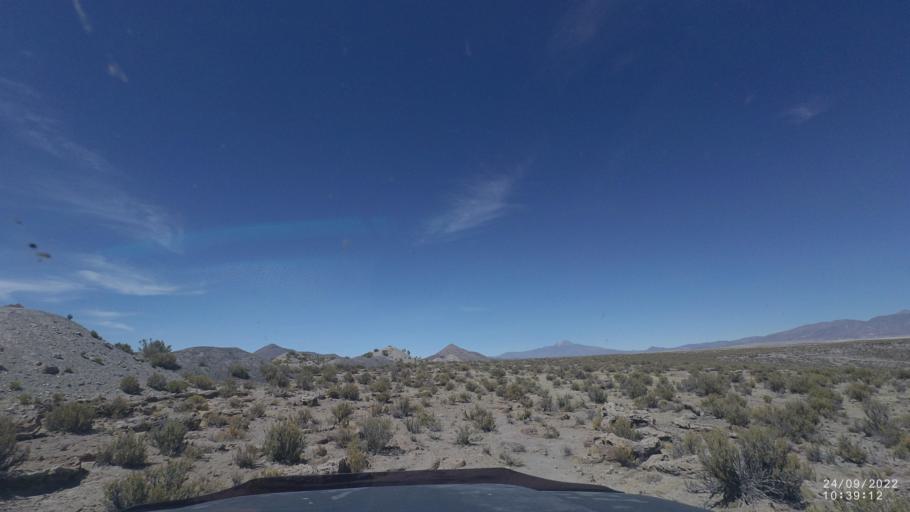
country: BO
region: Oruro
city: Challapata
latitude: -19.4672
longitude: -67.4275
